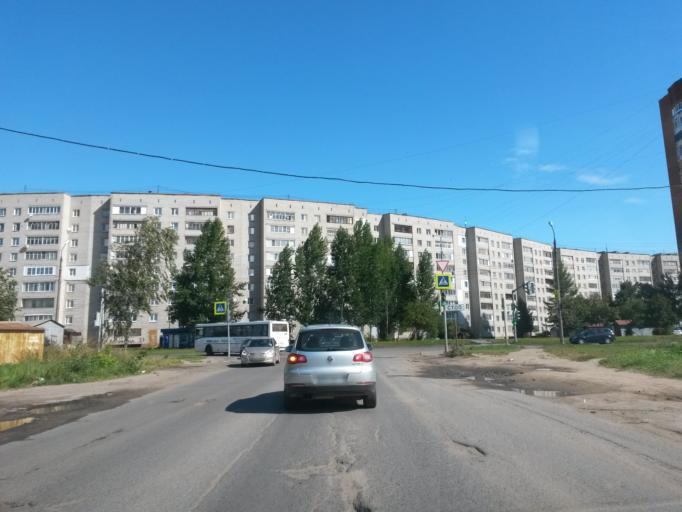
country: RU
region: Jaroslavl
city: Yaroslavl
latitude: 57.5694
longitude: 39.8608
